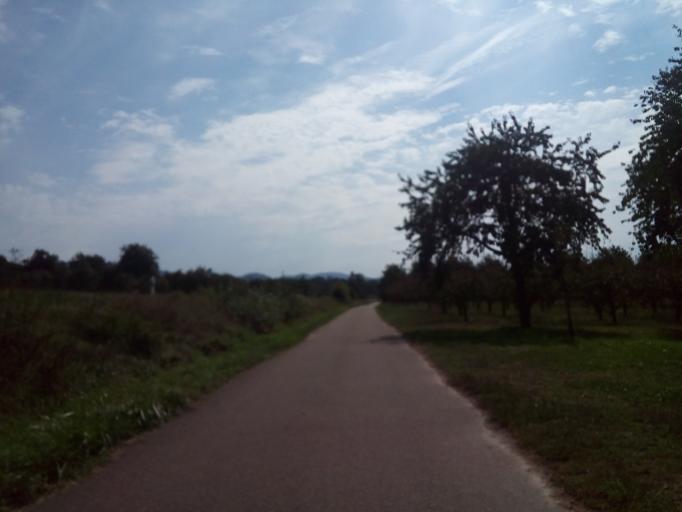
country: DE
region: Baden-Wuerttemberg
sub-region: Freiburg Region
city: Sasbach
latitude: 48.6547
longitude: 8.0979
